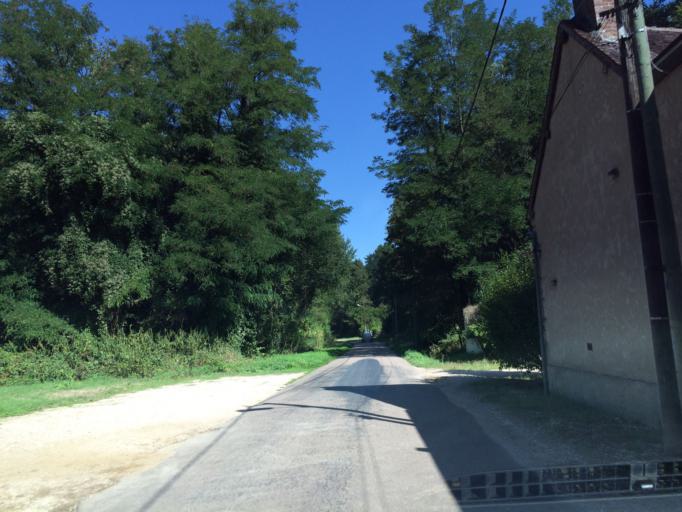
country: FR
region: Bourgogne
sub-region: Departement de l'Yonne
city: Fleury-la-Vallee
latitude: 47.8518
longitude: 3.3998
